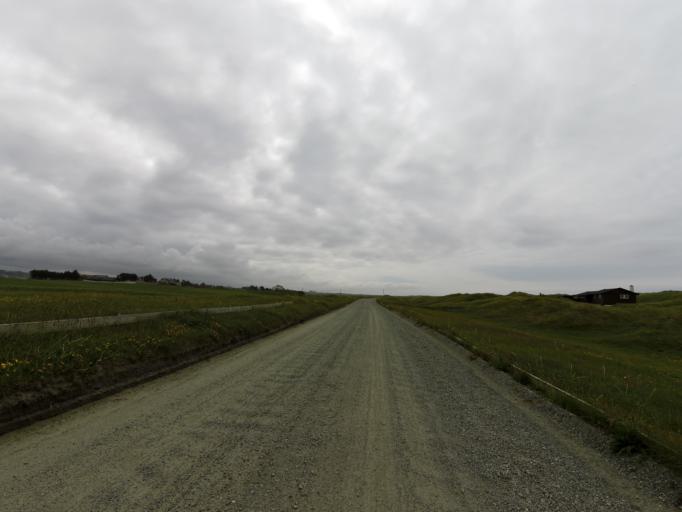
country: NO
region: Rogaland
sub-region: Klepp
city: Kleppe
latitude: 58.8068
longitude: 5.5512
